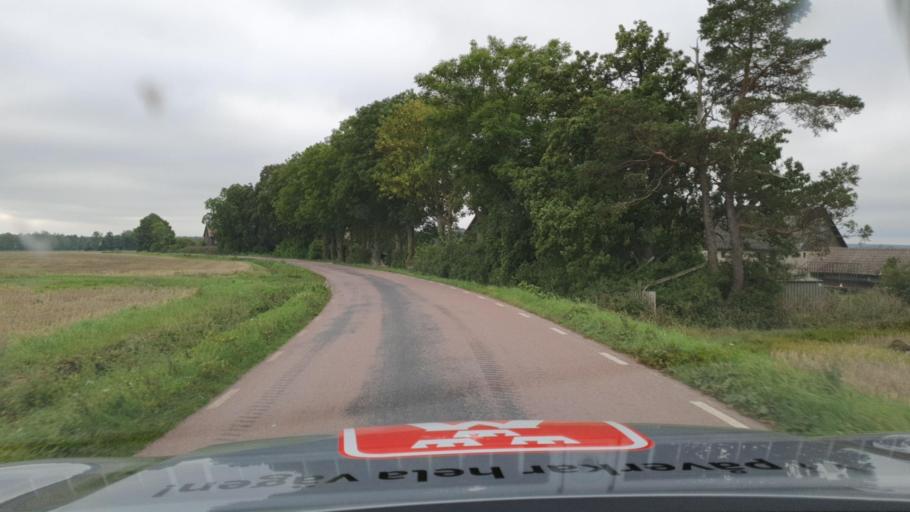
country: SE
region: Gotland
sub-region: Gotland
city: Visby
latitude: 57.6046
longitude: 18.4585
